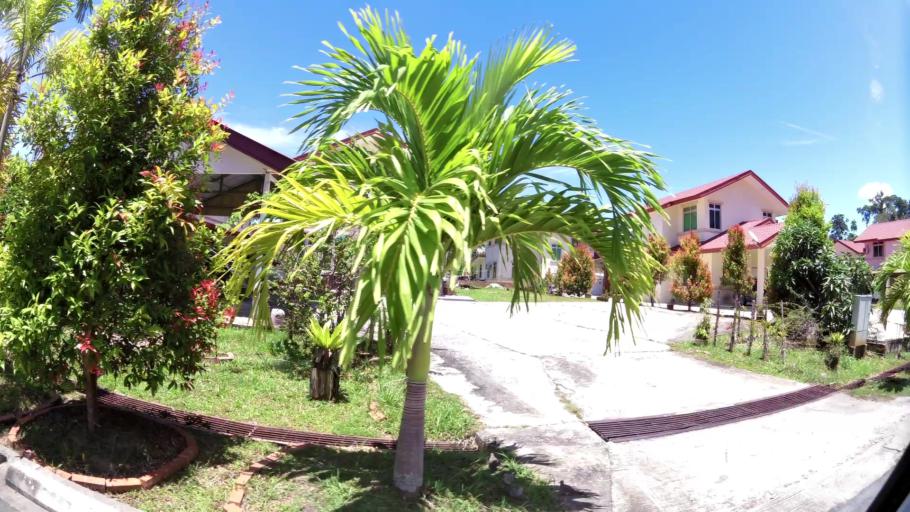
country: BN
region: Brunei and Muara
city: Bandar Seri Begawan
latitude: 5.0156
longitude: 115.0304
